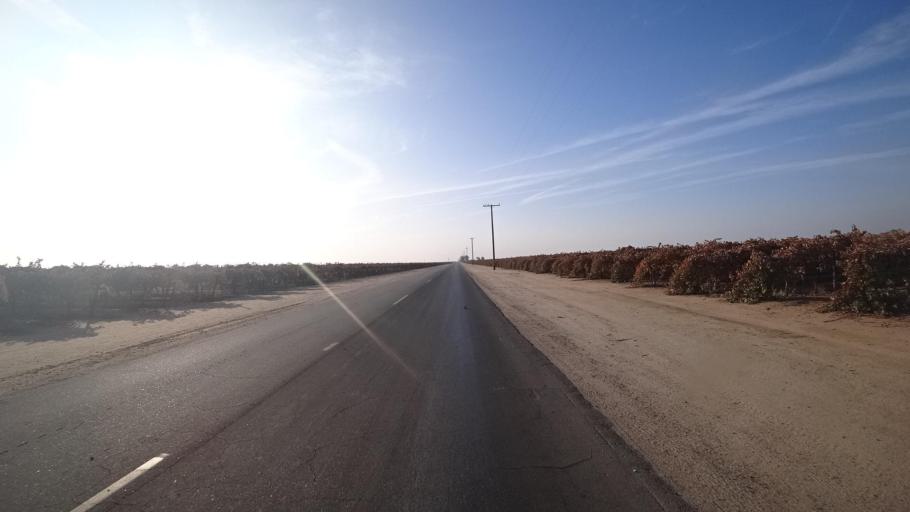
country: US
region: California
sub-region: Kern County
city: Delano
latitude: 35.7578
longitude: -119.1874
